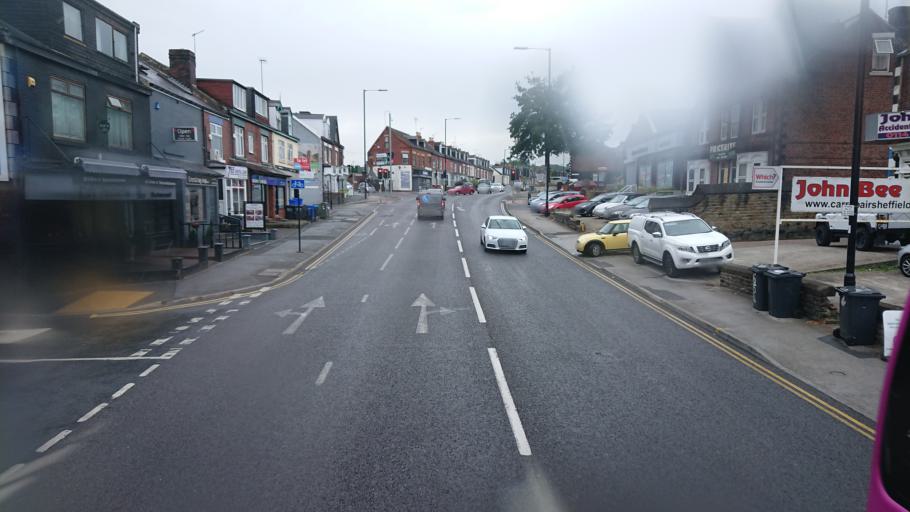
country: GB
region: England
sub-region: Sheffield
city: Sheffield
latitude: 53.3536
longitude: -1.4859
